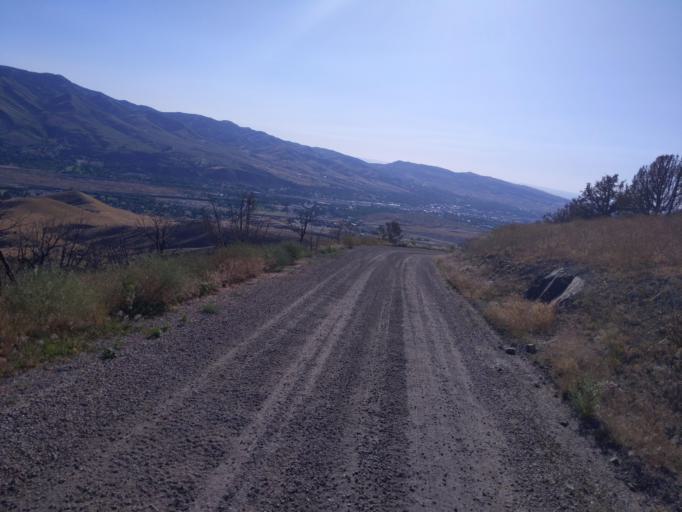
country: US
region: Idaho
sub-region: Bannock County
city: Pocatello
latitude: 42.8497
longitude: -112.3769
